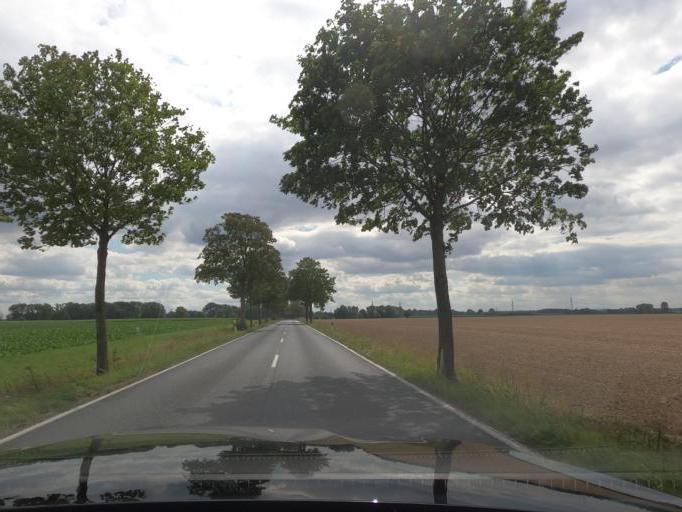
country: DE
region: Lower Saxony
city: Lehrte
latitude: 52.3510
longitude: 10.0280
